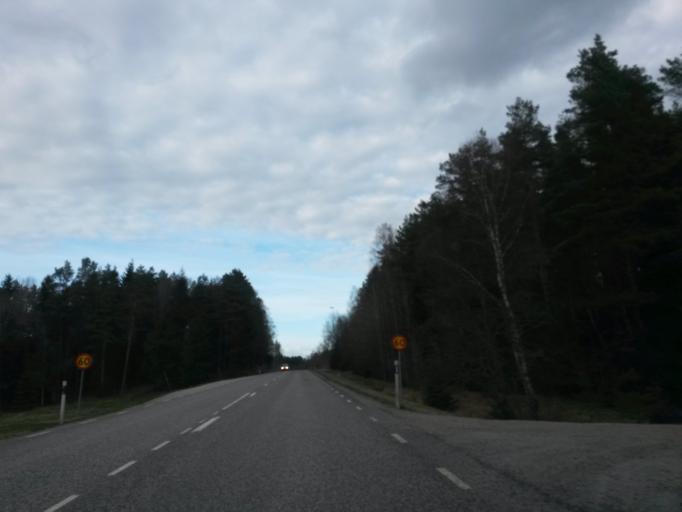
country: SE
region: Vaestra Goetaland
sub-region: Vargarda Kommun
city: Jonstorp
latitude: 58.0621
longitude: 12.6785
